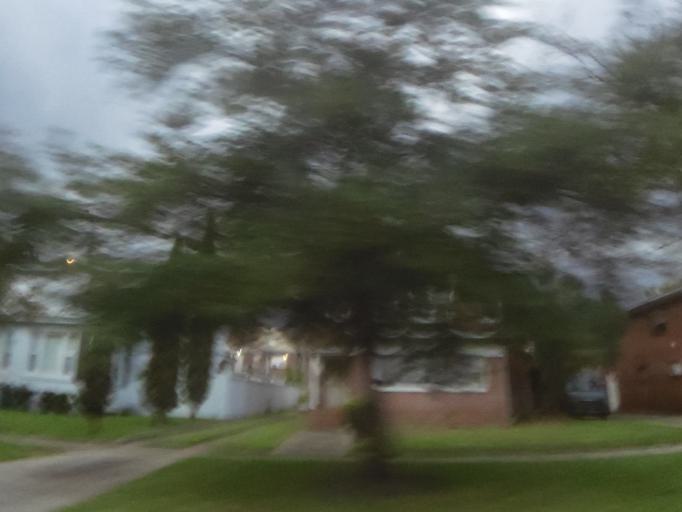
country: US
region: Florida
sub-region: Duval County
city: Jacksonville
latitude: 30.3066
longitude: -81.6958
